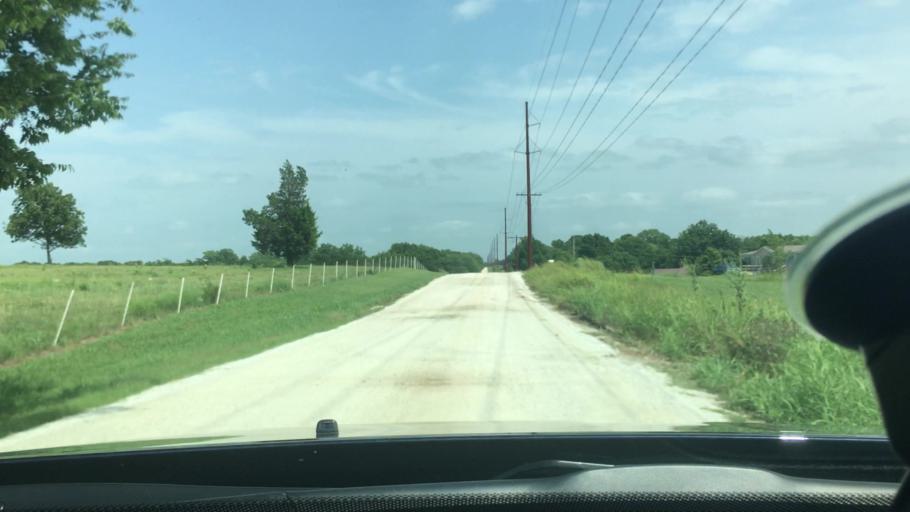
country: US
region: Oklahoma
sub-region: Pontotoc County
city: Ada
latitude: 34.8255
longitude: -96.7437
